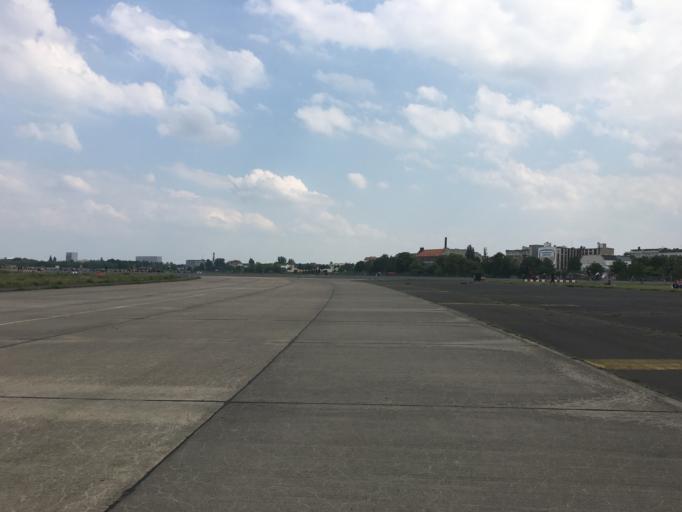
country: DE
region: Berlin
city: Tempelhof Bezirk
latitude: 52.4719
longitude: 13.3905
